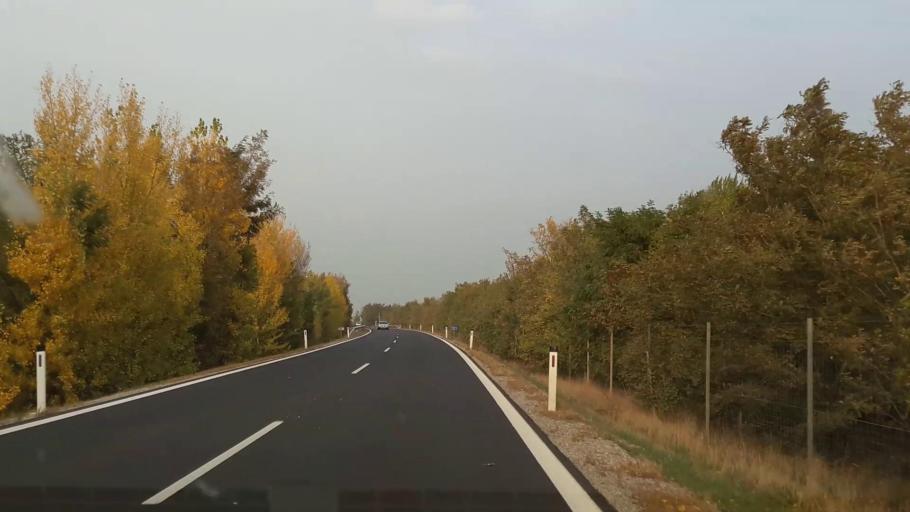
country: AT
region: Burgenland
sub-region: Politischer Bezirk Neusiedl am See
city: Gols
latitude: 47.9295
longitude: 16.9131
